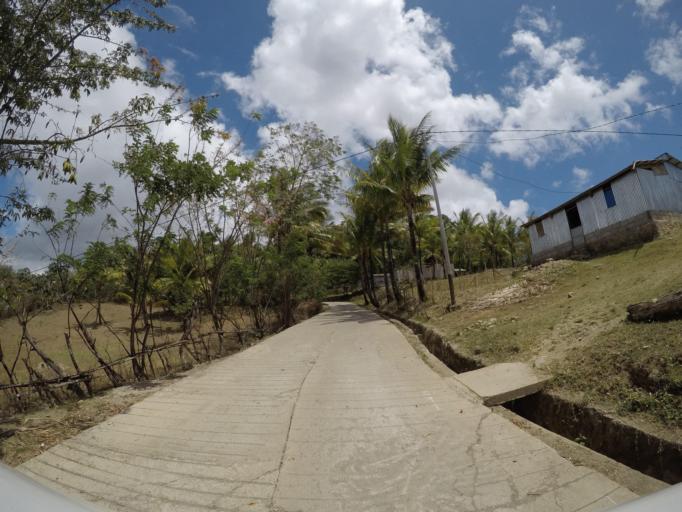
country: TL
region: Lautem
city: Lospalos
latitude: -8.5467
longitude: 126.8324
